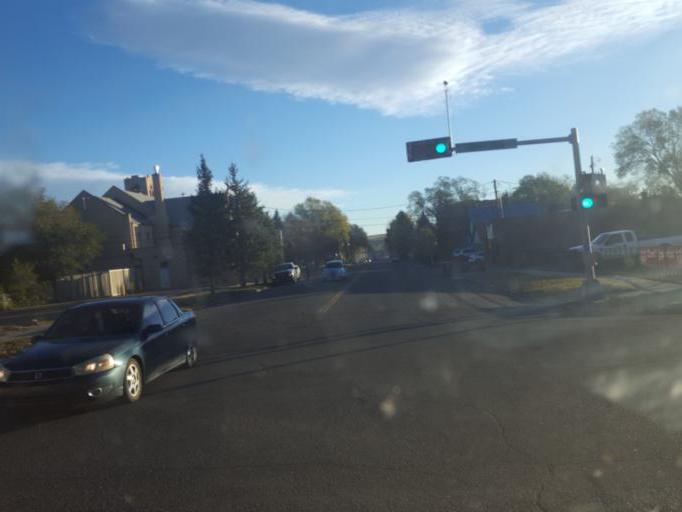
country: US
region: New Mexico
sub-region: San Miguel County
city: Las Vegas
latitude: 35.5964
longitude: -105.2176
